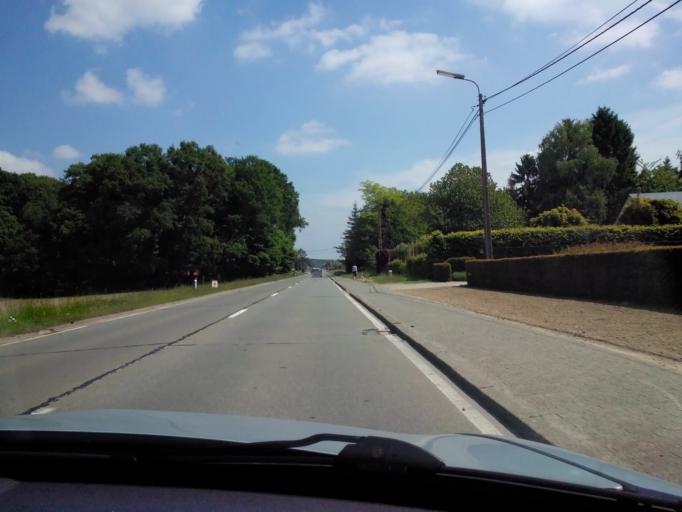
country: BE
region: Flanders
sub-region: Provincie Vlaams-Brabant
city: Holsbeek
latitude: 50.9559
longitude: 4.7655
